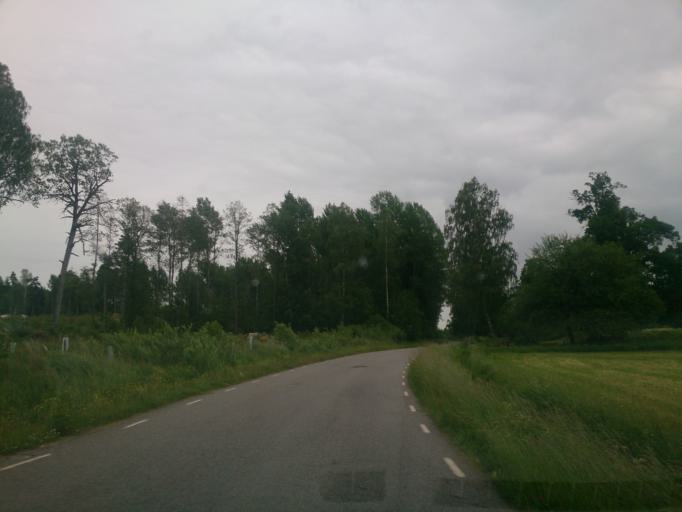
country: SE
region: OEstergoetland
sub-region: Atvidabergs Kommun
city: Atvidaberg
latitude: 58.2795
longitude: 16.1018
